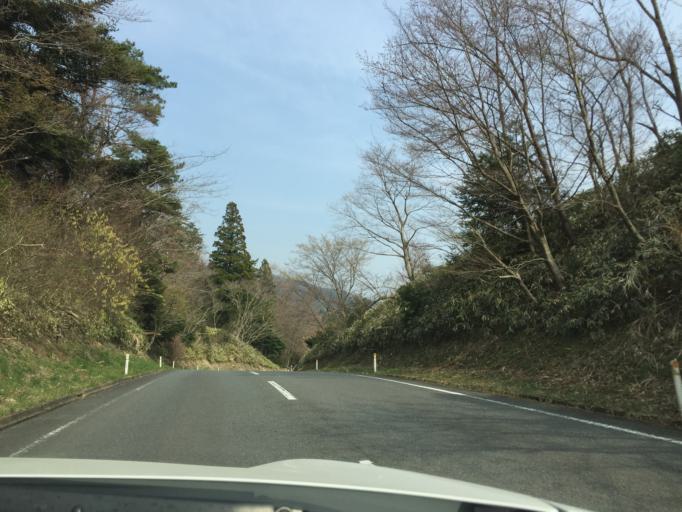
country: JP
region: Fukushima
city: Iwaki
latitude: 37.0279
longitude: 140.7456
